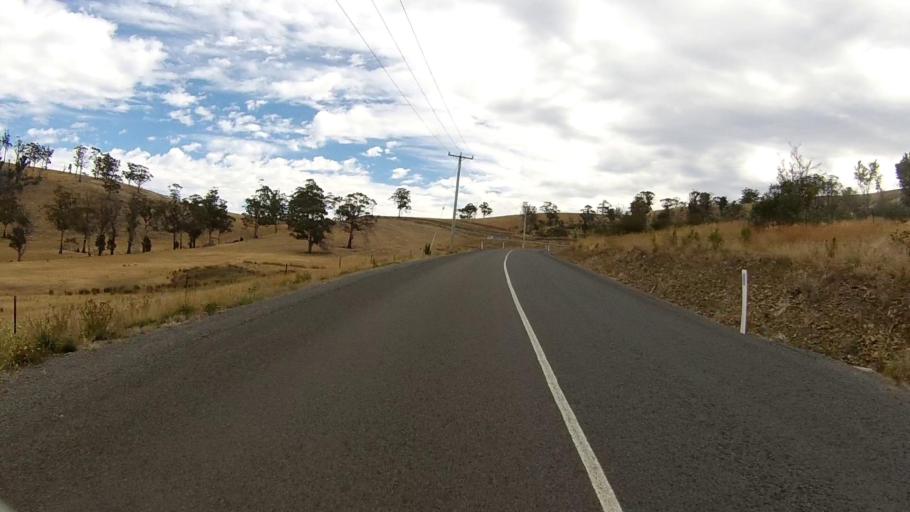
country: AU
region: Tasmania
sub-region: Sorell
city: Sorell
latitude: -42.8843
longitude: 147.7194
